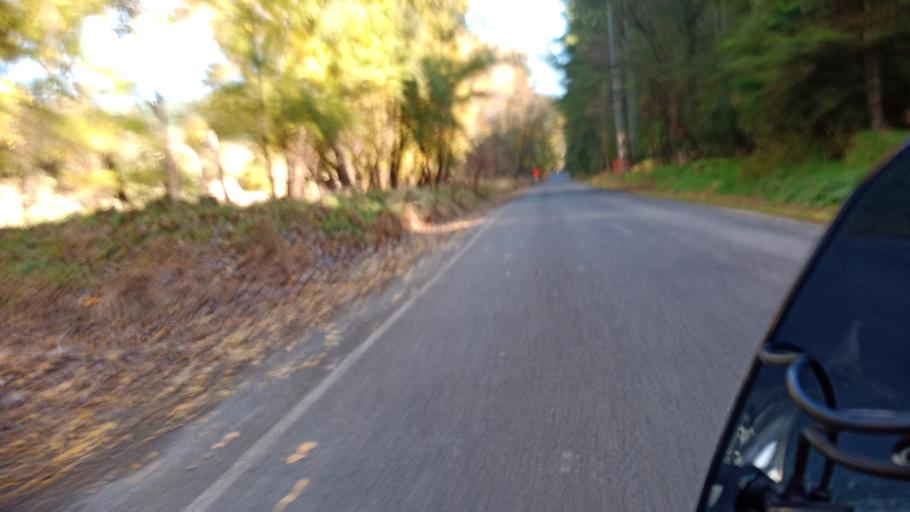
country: NZ
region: Hawke's Bay
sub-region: Wairoa District
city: Wairoa
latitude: -38.9206
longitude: 177.2486
